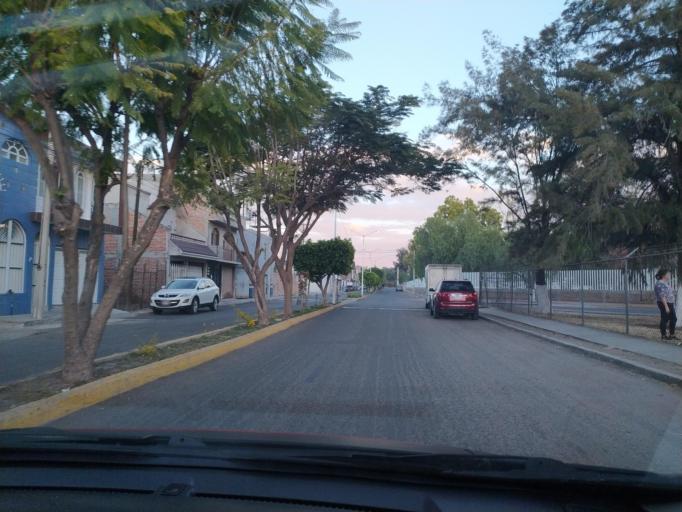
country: MX
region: Guanajuato
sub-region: San Francisco del Rincon
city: Fraccionamiento la Mezquitera
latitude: 21.0104
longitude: -101.8417
